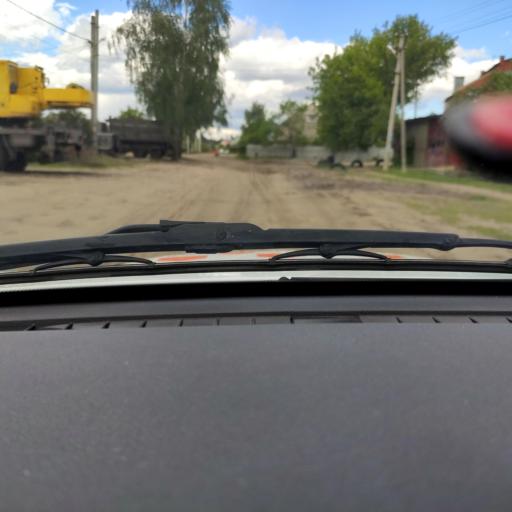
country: RU
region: Voronezj
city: Podgornoye
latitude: 51.7423
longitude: 39.1581
